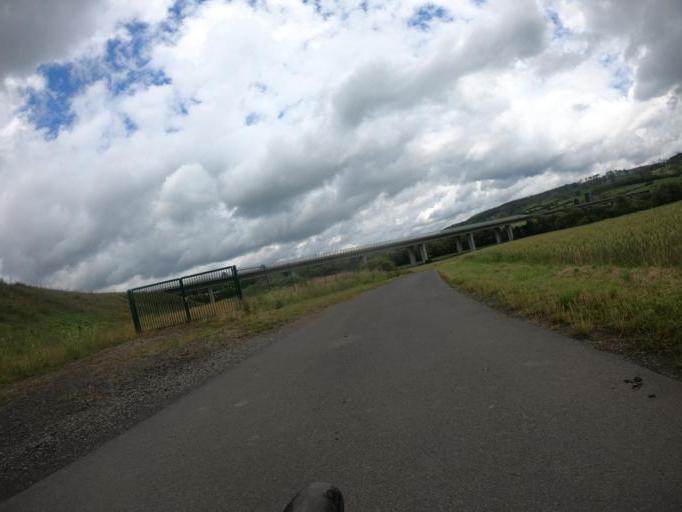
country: DE
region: Hesse
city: Hessisch Lichtenau
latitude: 51.1928
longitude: 9.7795
